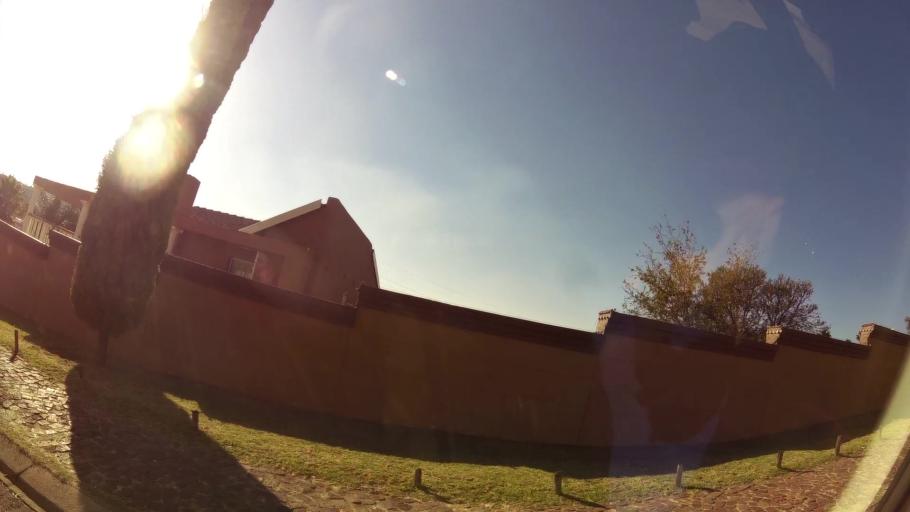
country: ZA
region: Gauteng
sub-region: City of Johannesburg Metropolitan Municipality
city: Johannesburg
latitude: -26.2706
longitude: 28.0517
